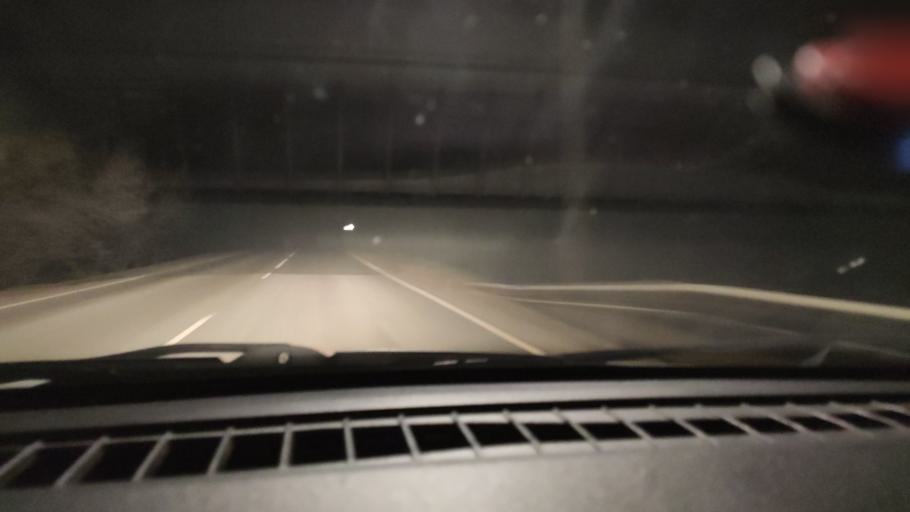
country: RU
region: Bashkortostan
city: Yermolayevo
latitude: 52.6546
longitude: 55.8348
